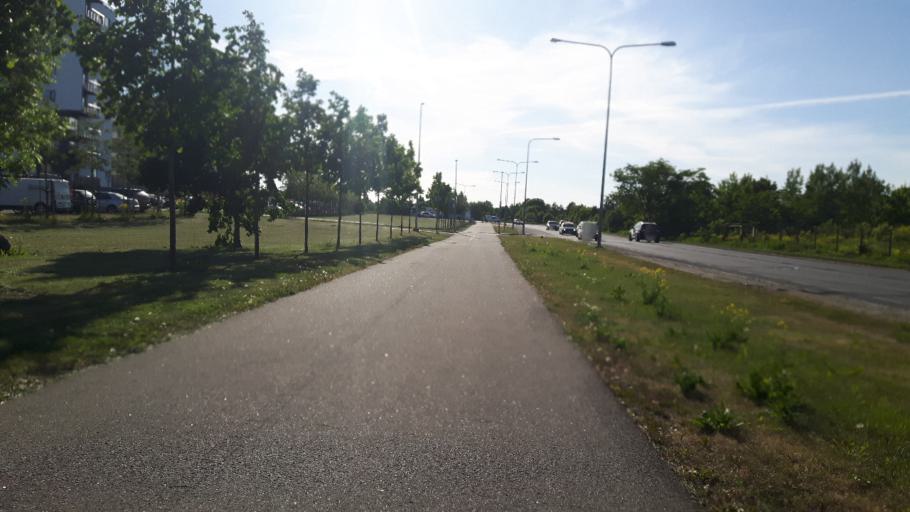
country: EE
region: Harju
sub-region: Tallinna linn
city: Kose
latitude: 59.4520
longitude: 24.8375
